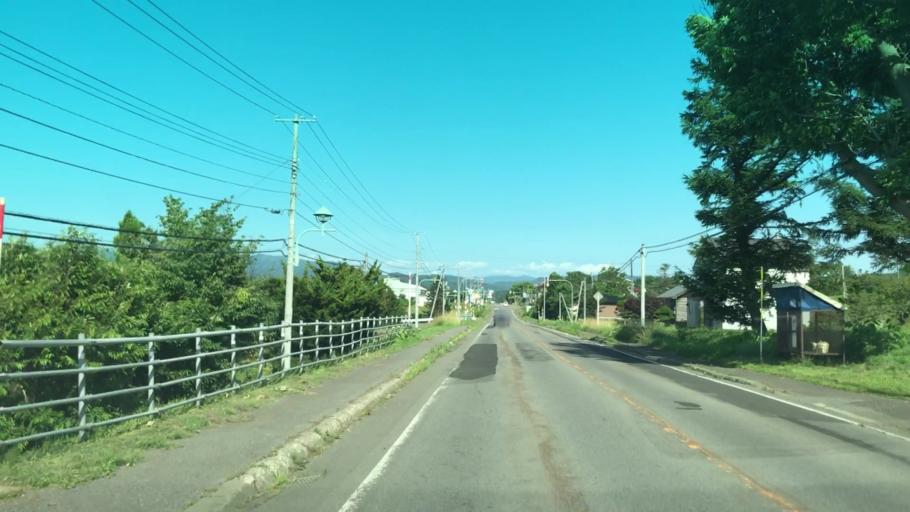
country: JP
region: Hokkaido
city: Iwanai
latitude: 42.9800
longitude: 140.6007
